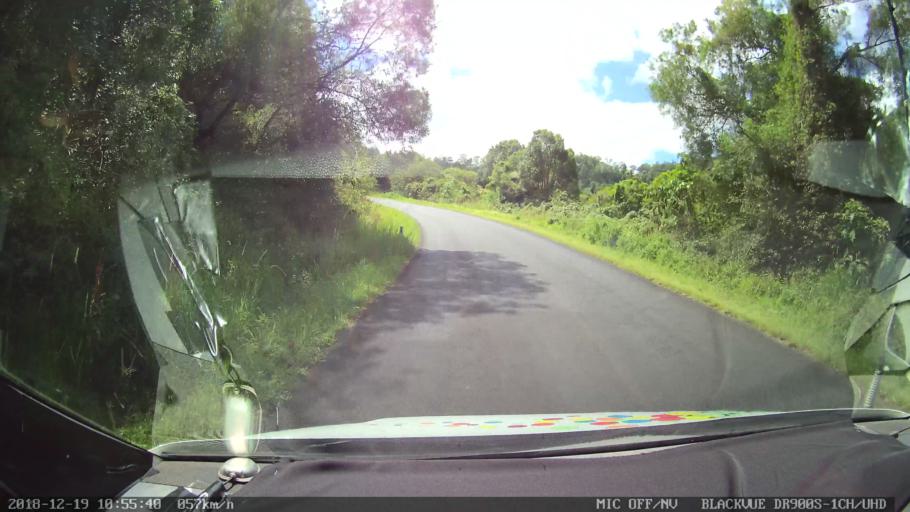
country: AU
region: New South Wales
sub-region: Lismore Municipality
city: Nimbin
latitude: -28.5959
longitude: 153.2560
